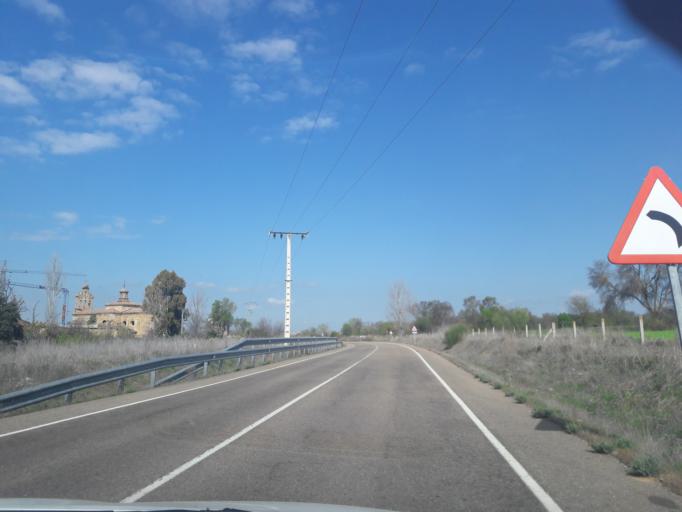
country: ES
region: Castille and Leon
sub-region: Provincia de Salamanca
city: Ciudad Rodrigo
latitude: 40.5728
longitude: -6.4912
